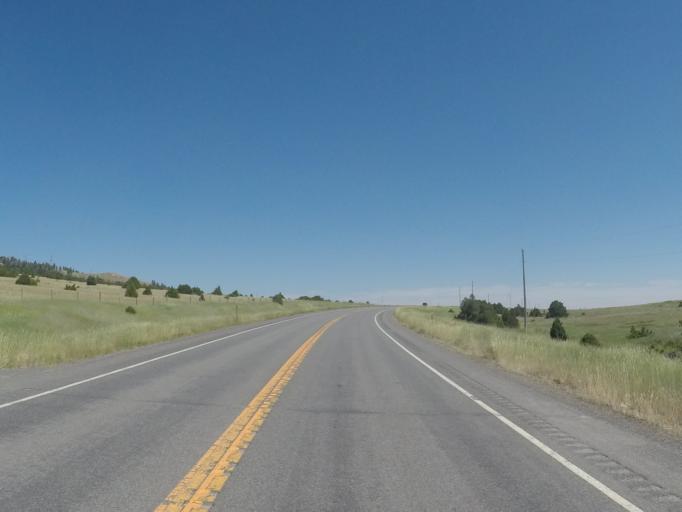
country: US
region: Montana
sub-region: Lewis and Clark County
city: East Helena
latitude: 46.5327
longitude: -111.7210
